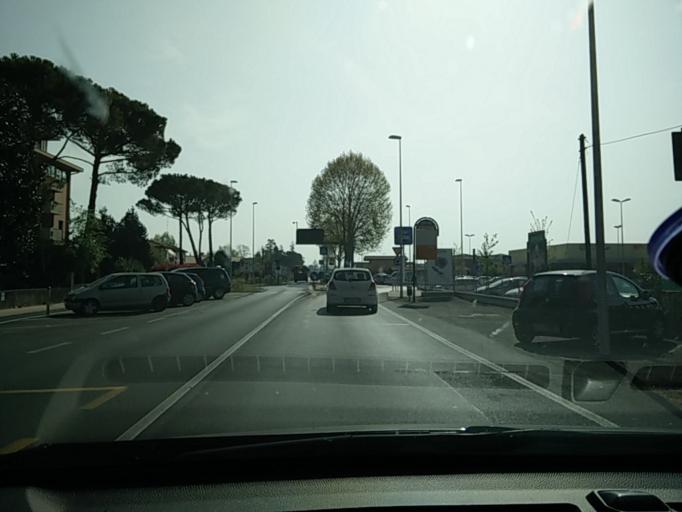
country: IT
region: Friuli Venezia Giulia
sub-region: Provincia di Pordenone
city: Pordenone
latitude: 45.9481
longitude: 12.6809
